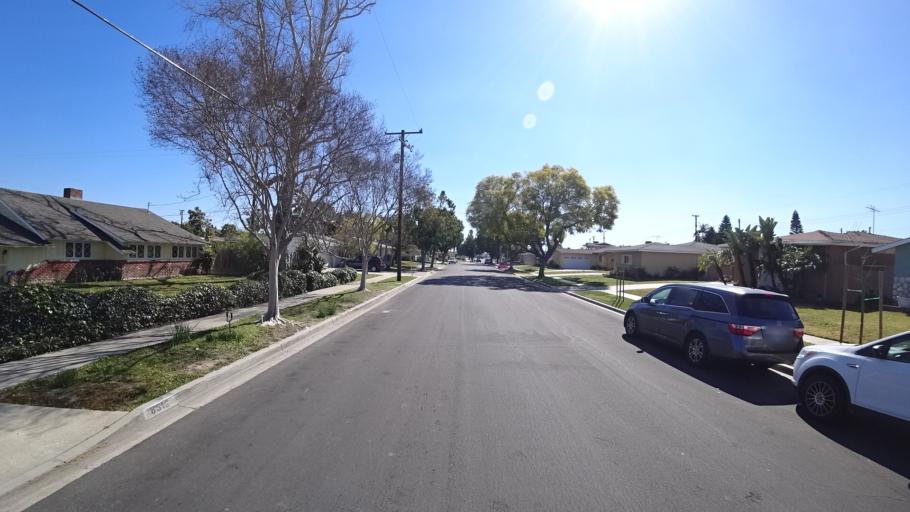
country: US
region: California
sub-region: Orange County
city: Buena Park
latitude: 33.8378
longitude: -117.9865
